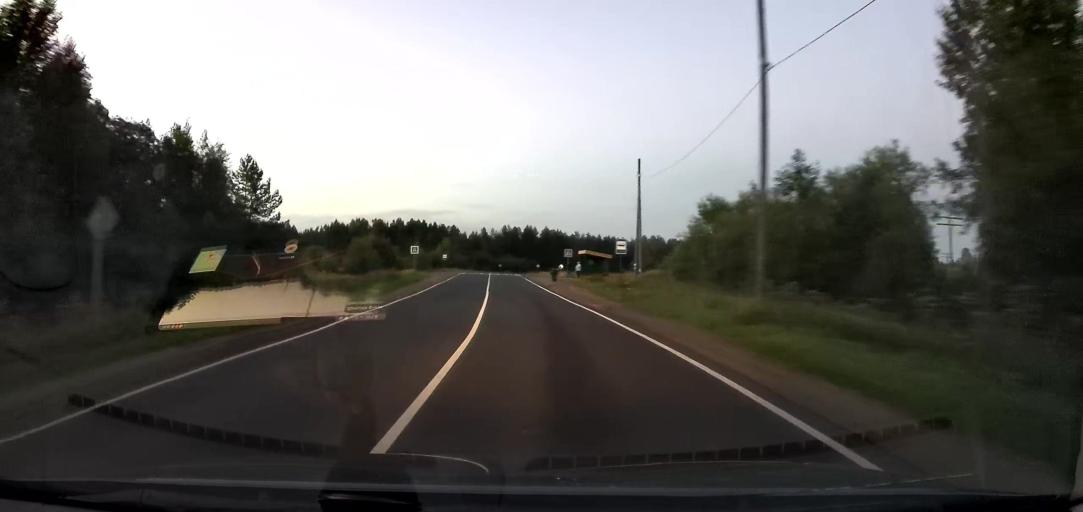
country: RU
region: Arkhangelskaya
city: Uyemskiy
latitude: 64.4150
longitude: 40.9927
